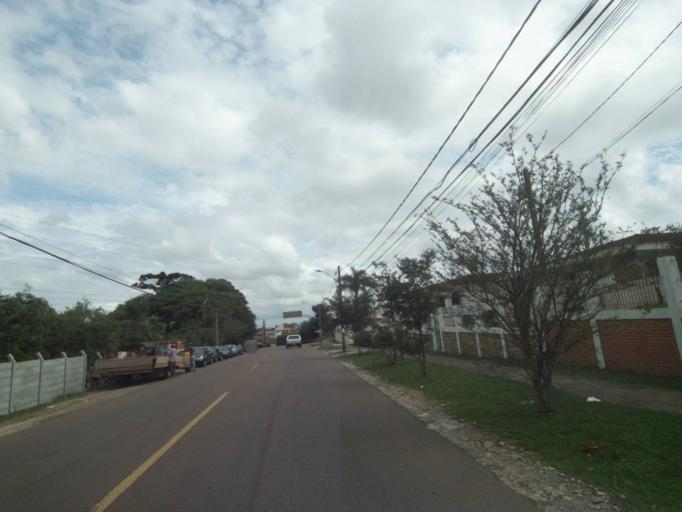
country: BR
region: Parana
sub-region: Curitiba
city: Curitiba
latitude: -25.3842
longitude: -49.2798
